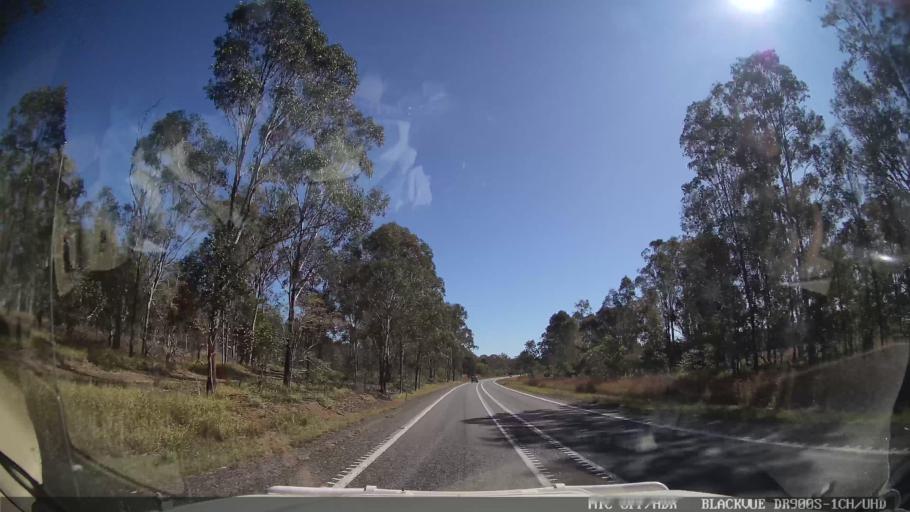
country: AU
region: Queensland
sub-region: Gympie Regional Council
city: Gympie
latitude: -26.0467
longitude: 152.5745
